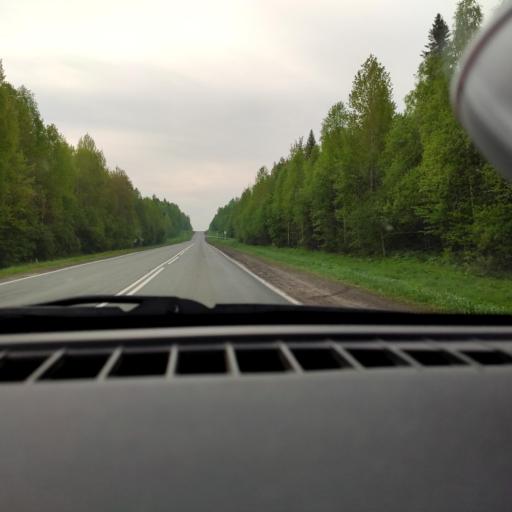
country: RU
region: Perm
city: Perm
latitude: 58.1575
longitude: 56.2491
